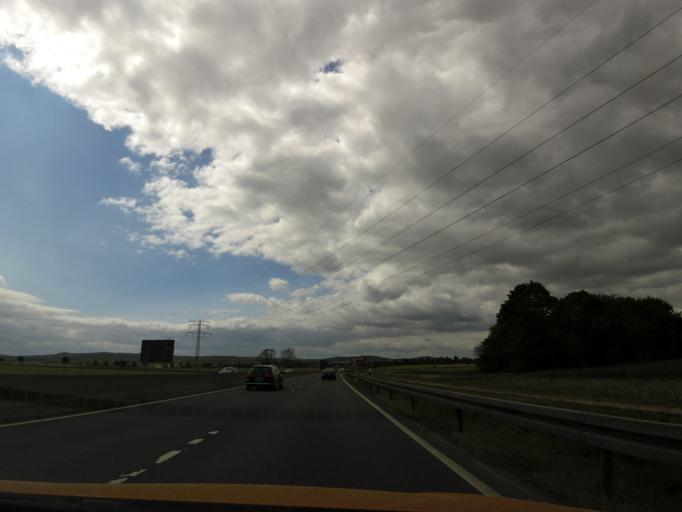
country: DE
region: Lower Saxony
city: Lengede
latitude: 52.1467
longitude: 10.3536
